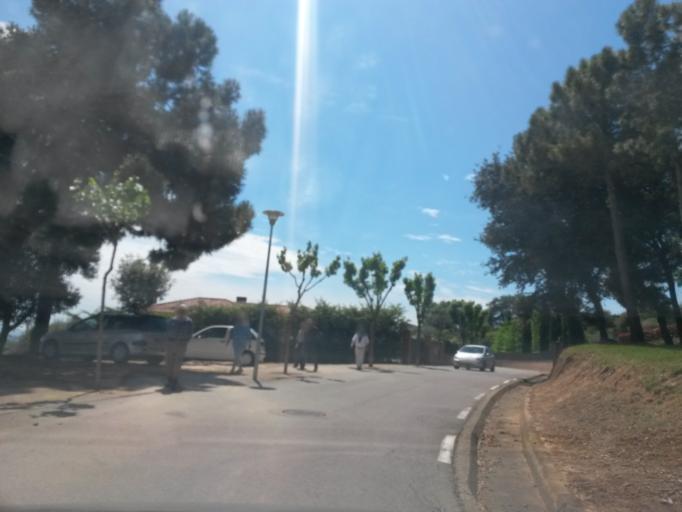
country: ES
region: Catalonia
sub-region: Provincia de Girona
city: Vilablareix
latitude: 41.9618
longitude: 2.7622
